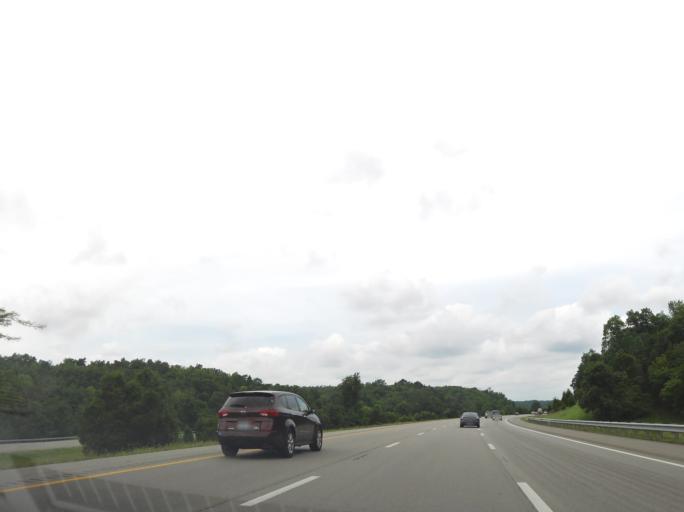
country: US
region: Kentucky
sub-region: Scott County
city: Georgetown
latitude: 38.3259
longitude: -84.5612
